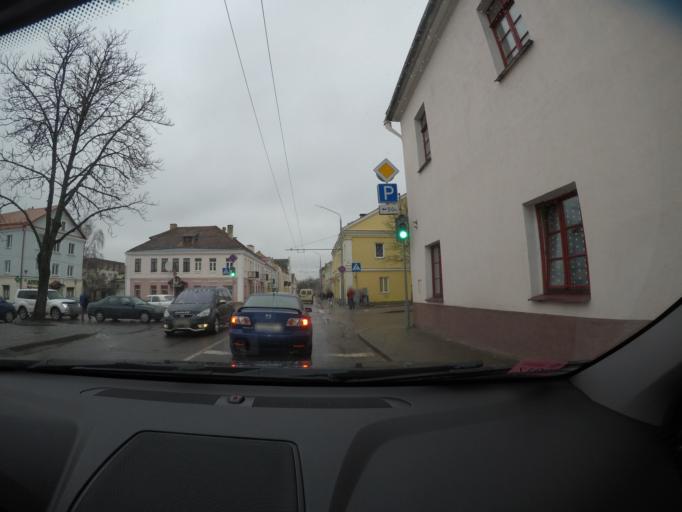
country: BY
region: Grodnenskaya
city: Hrodna
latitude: 53.6812
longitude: 23.8286
